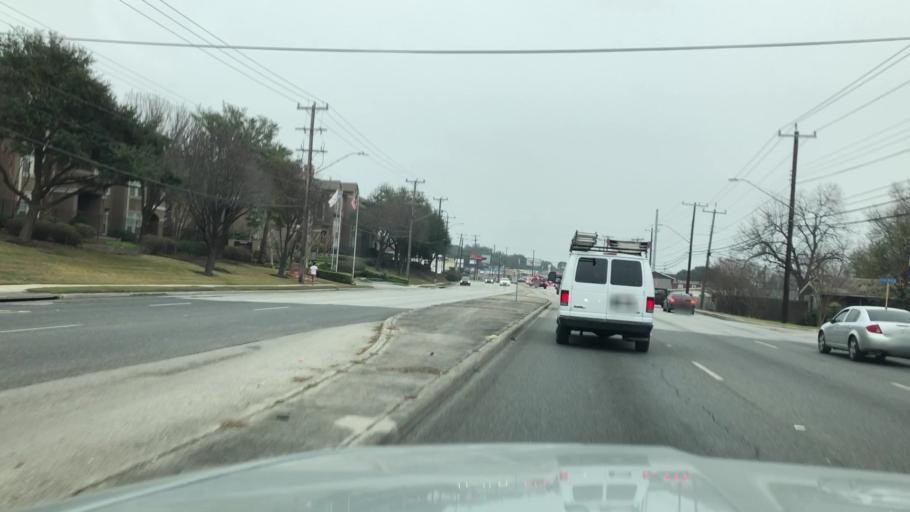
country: US
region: Texas
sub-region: Bexar County
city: Balcones Heights
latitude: 29.4957
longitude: -98.5727
